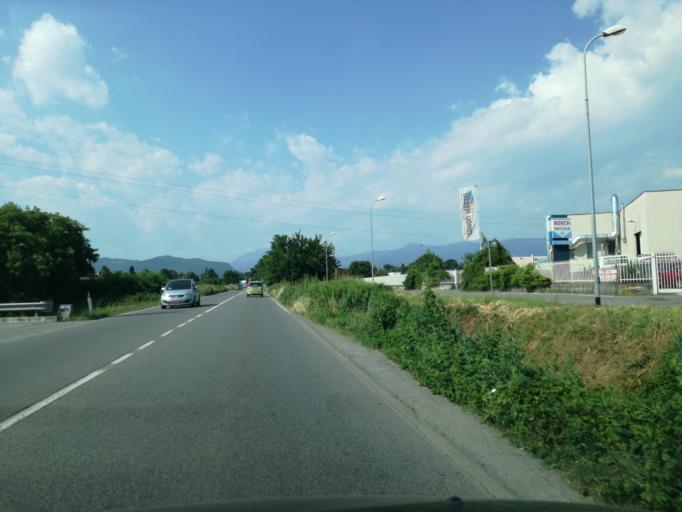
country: IT
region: Lombardy
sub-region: Provincia di Lecco
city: Cernusco Lombardone
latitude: 45.6851
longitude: 9.3991
